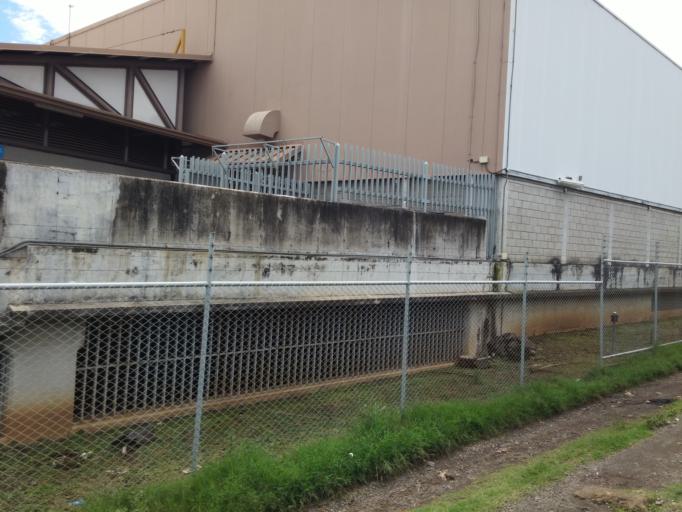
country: CR
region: Heredia
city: San Francisco
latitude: 9.9951
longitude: -84.1301
